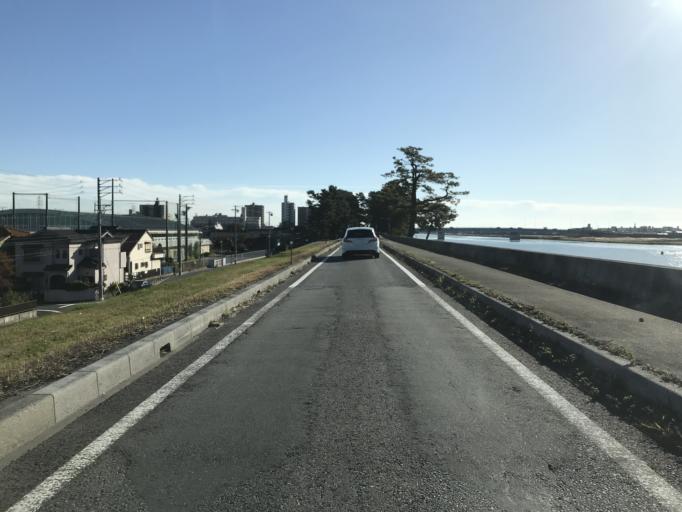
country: JP
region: Aichi
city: Kanie
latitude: 35.1290
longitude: 136.8388
